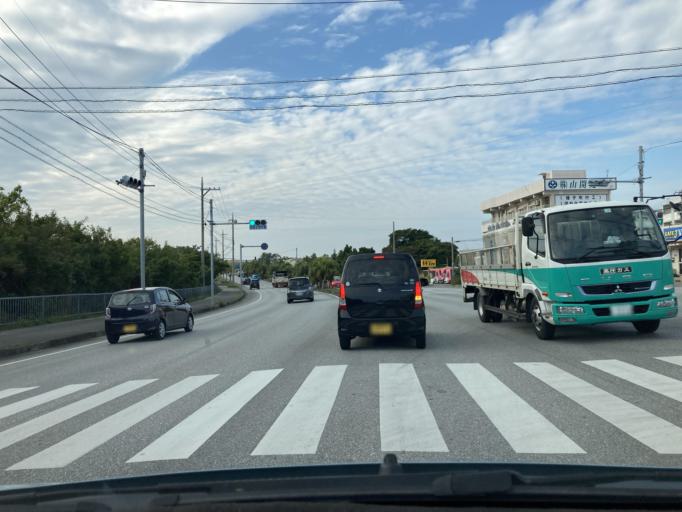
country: JP
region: Okinawa
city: Okinawa
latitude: 26.3597
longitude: 127.7997
